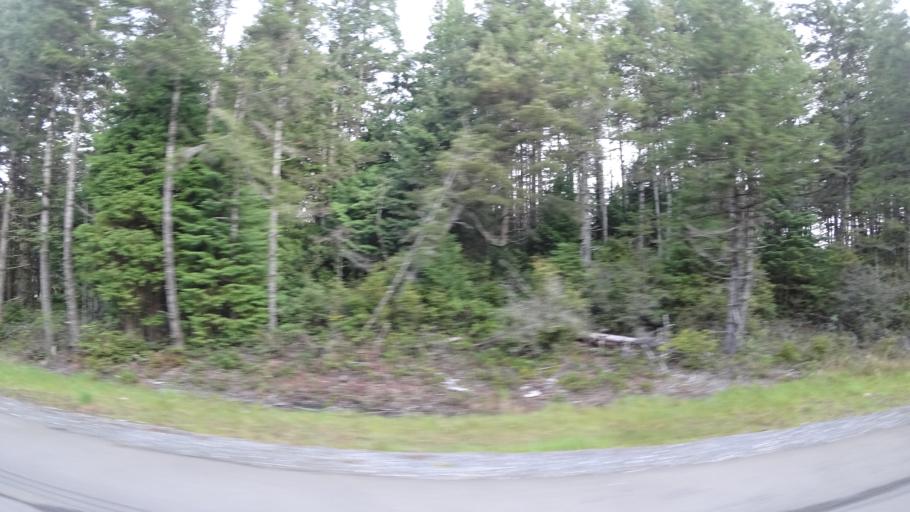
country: US
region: Oregon
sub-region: Coos County
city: Bandon
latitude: 43.1744
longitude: -124.3715
